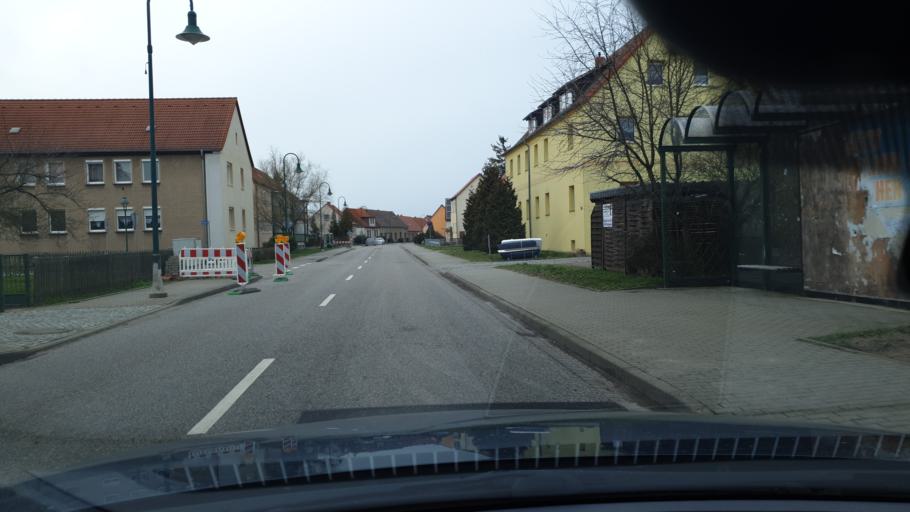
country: DE
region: Saxony-Anhalt
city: Vockerode
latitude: 51.8445
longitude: 12.3535
